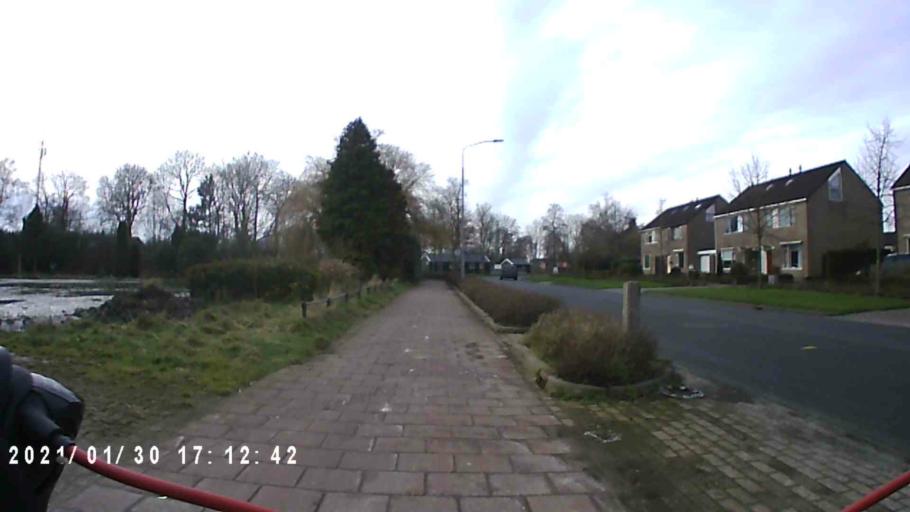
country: NL
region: Groningen
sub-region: Gemeente Leek
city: Leek
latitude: 53.1700
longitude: 6.3575
